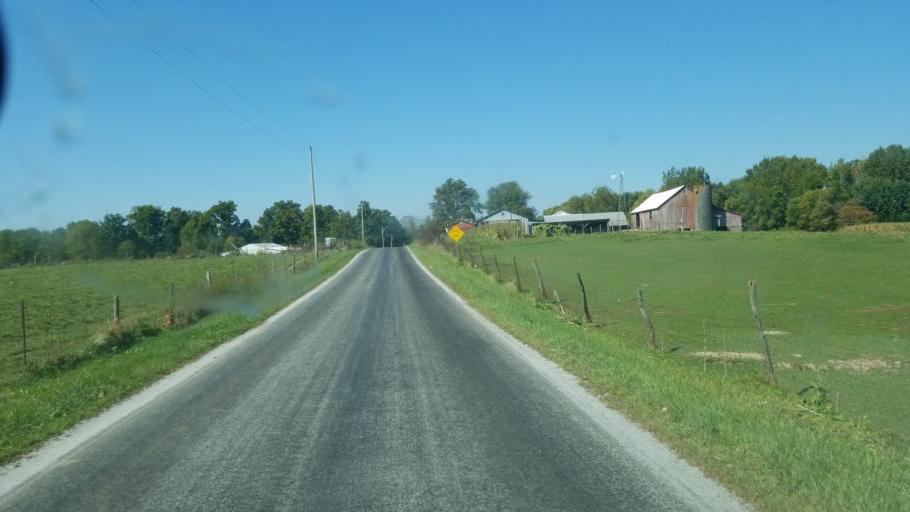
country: US
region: Ohio
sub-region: Hardin County
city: Kenton
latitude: 40.6185
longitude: -83.4952
